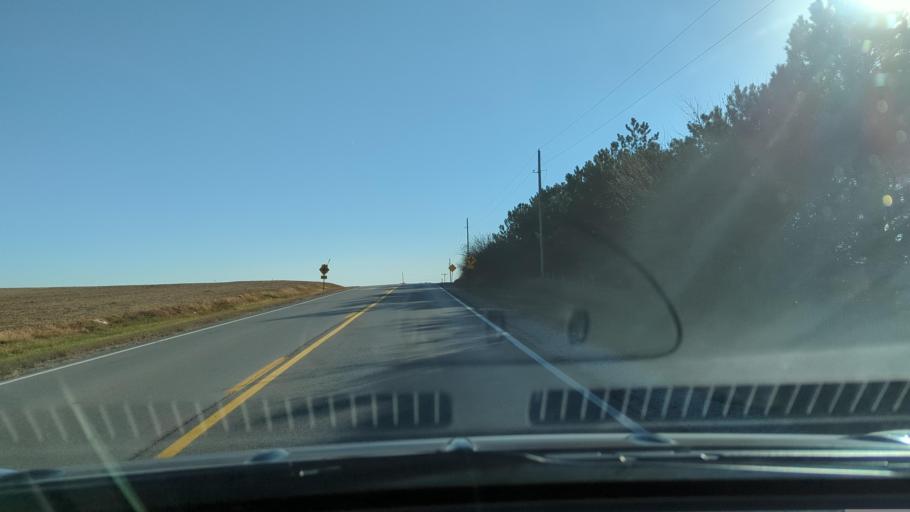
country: US
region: Nebraska
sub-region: Sarpy County
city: Springfield
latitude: 41.0890
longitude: -96.1038
